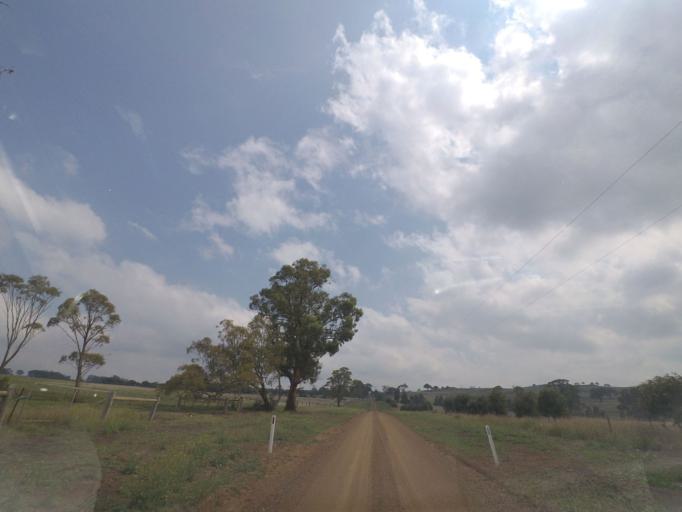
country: AU
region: Victoria
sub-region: Melton
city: Melton West
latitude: -37.6102
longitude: 144.5678
